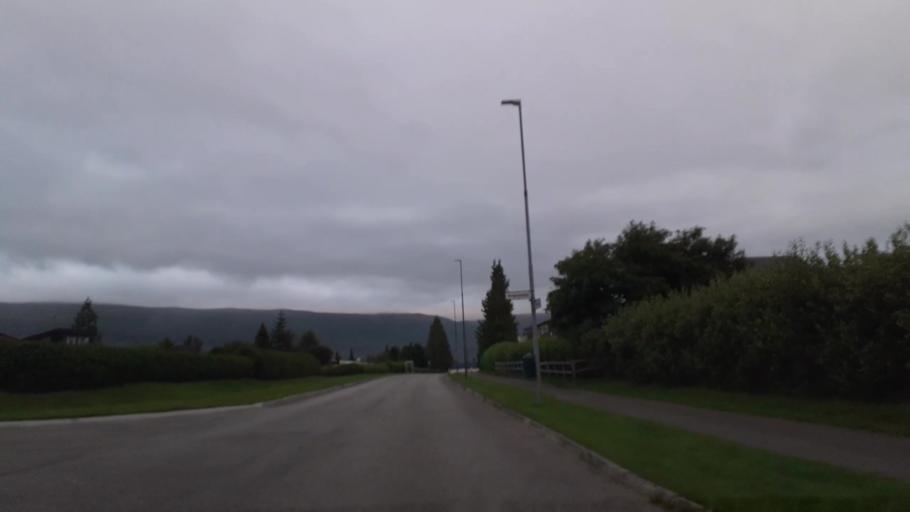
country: IS
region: Northeast
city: Akureyri
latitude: 65.6957
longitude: -18.1397
